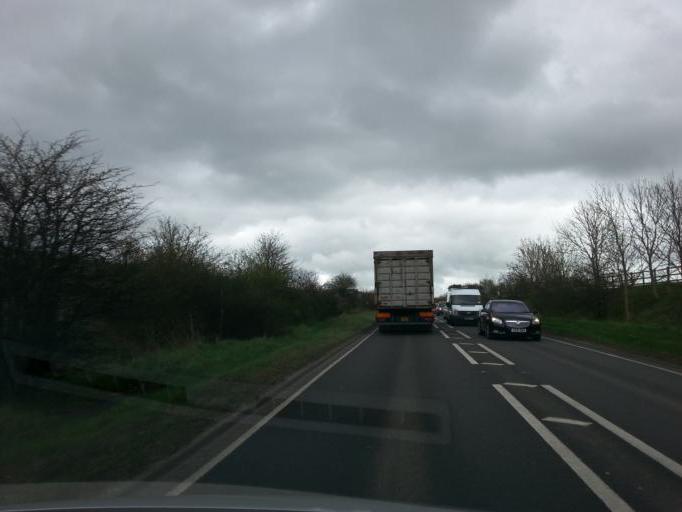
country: GB
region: England
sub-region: Wiltshire
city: Amesbury
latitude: 51.1775
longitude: -1.8152
